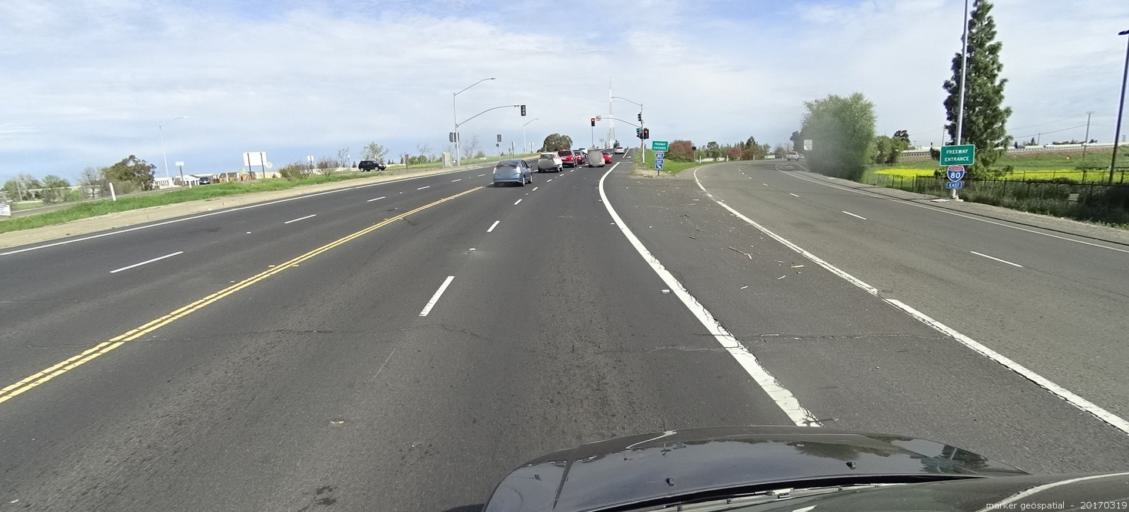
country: US
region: California
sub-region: Sacramento County
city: Sacramento
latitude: 38.6382
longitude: -121.4776
